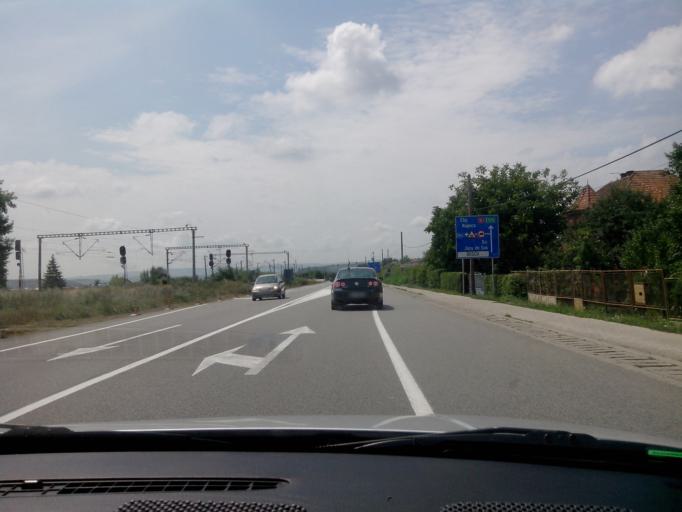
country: RO
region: Cluj
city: Jucu Herghelia
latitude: 46.8614
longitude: 23.7624
